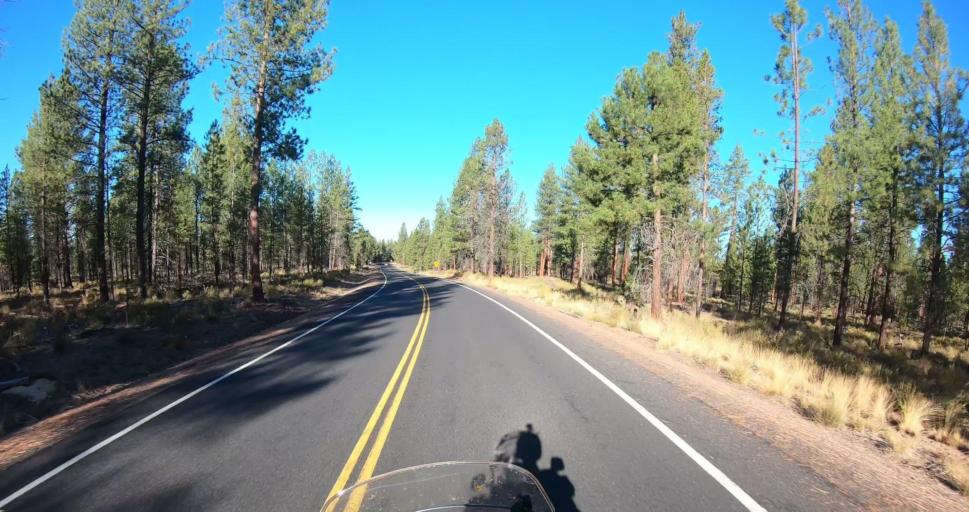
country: US
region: Oregon
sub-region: Deschutes County
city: La Pine
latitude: 43.7353
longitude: -121.4443
